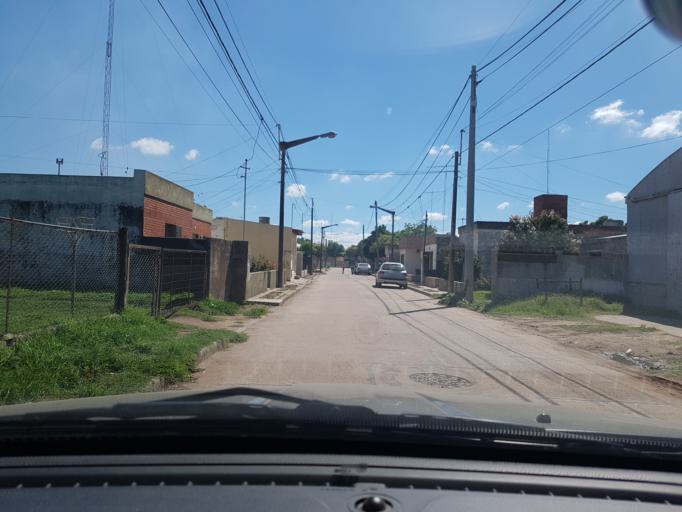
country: AR
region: Cordoba
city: General Cabrera
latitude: -32.7602
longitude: -63.7932
